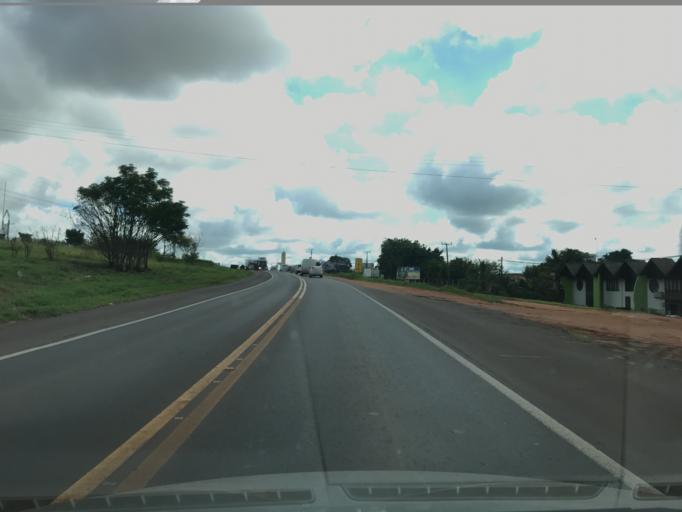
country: BR
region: Parana
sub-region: Umuarama
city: Umuarama
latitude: -23.8084
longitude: -53.3212
